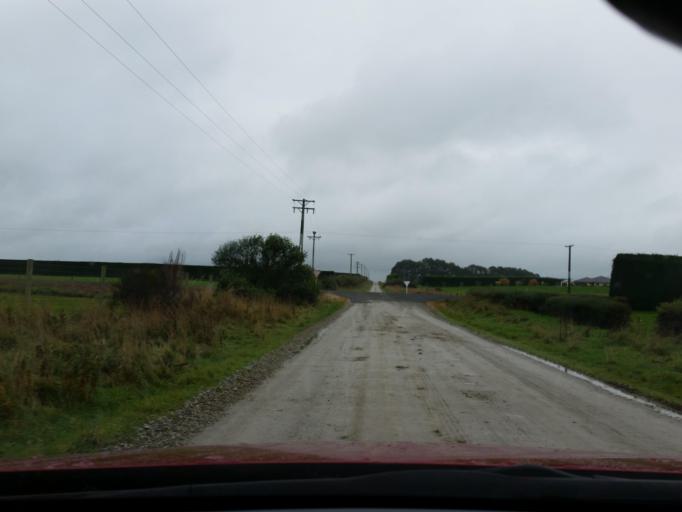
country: NZ
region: Southland
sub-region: Invercargill City
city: Invercargill
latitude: -46.2850
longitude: 168.4807
